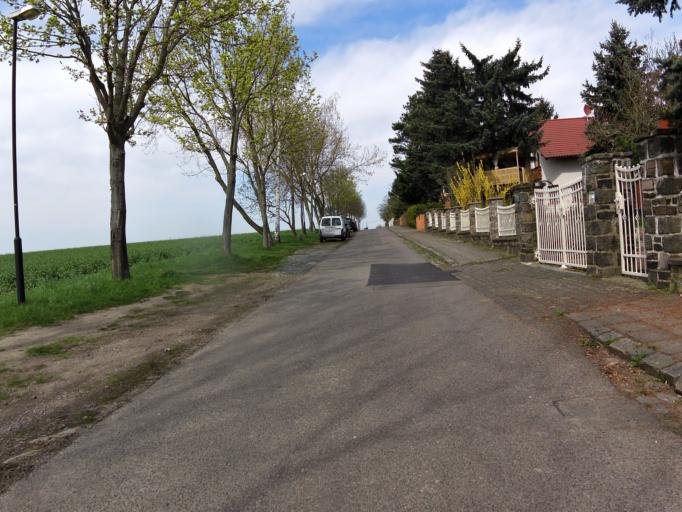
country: DE
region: Saxony
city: Schkeuditz
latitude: 51.3891
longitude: 12.2690
